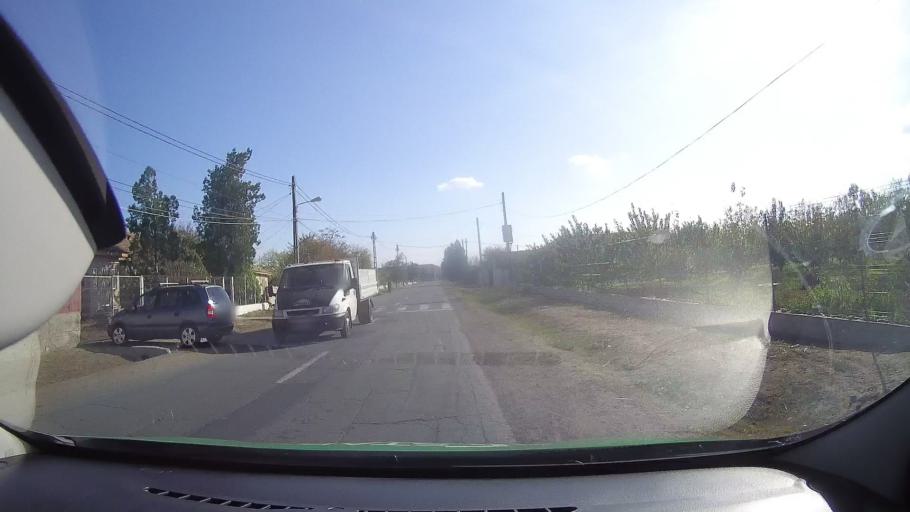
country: RO
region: Constanta
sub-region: Comuna Mihai Viteazu
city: Mihai Viteazu
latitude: 44.6310
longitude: 28.7297
